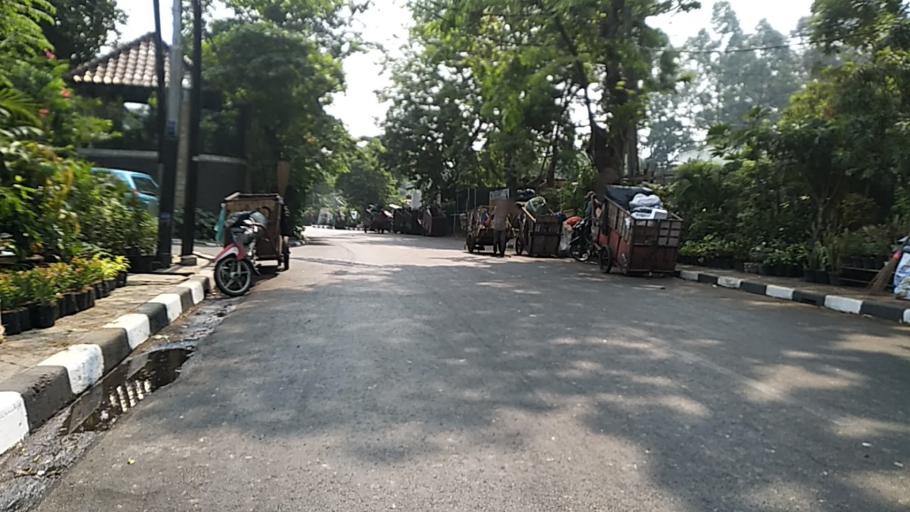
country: ID
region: Jakarta Raya
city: Jakarta
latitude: -6.2367
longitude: 106.8525
